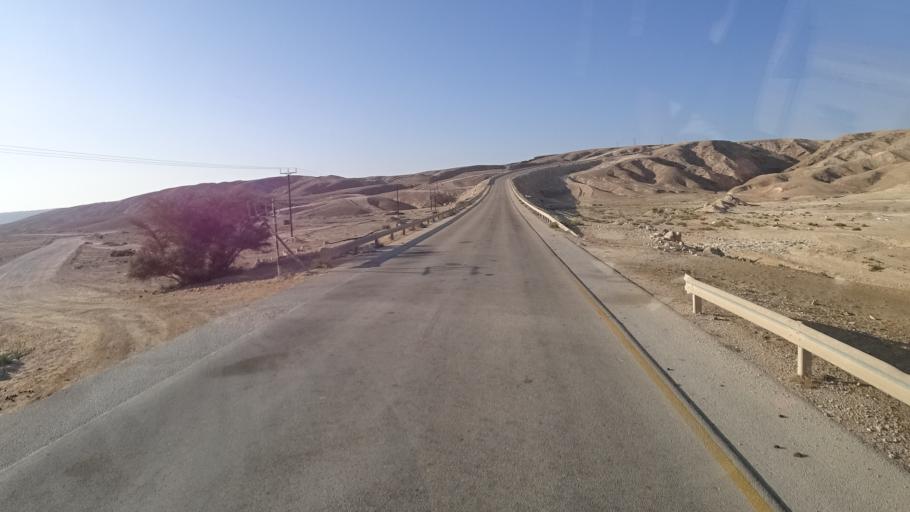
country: OM
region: Zufar
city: Salalah
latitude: 17.2418
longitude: 53.9155
